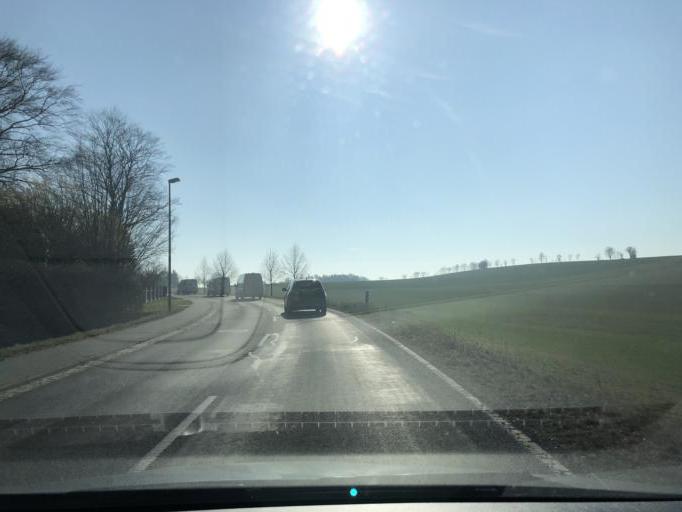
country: DE
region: Saxony
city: Hauswalde
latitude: 51.1526
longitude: 14.0943
